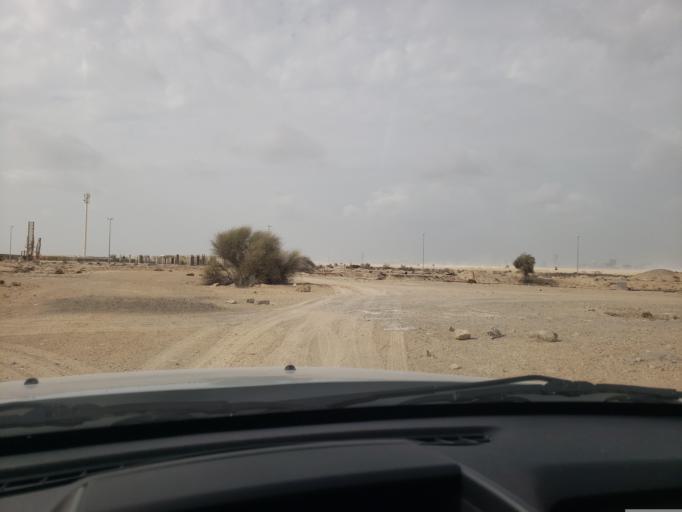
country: AE
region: Dubai
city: Dubai
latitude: 24.9990
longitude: 55.2405
